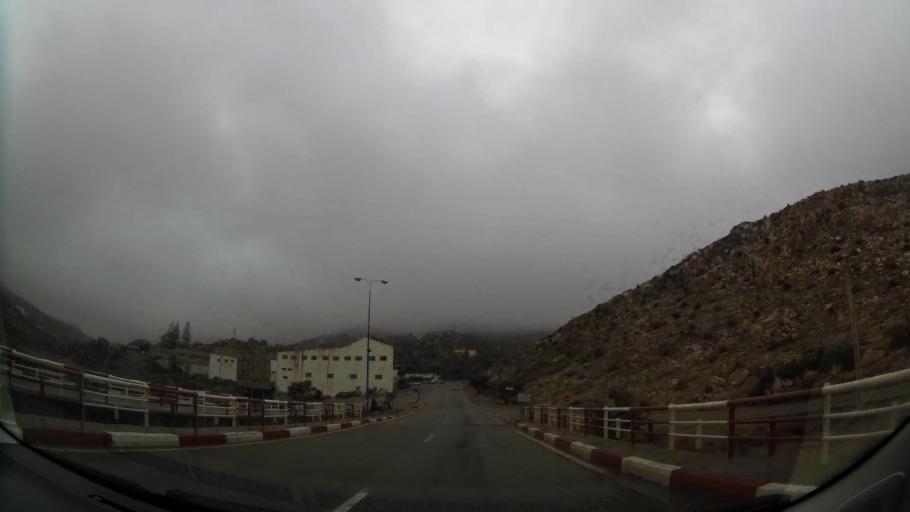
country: MA
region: Taza-Al Hoceima-Taounate
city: Al Hoceima
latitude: 35.2169
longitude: -3.9198
